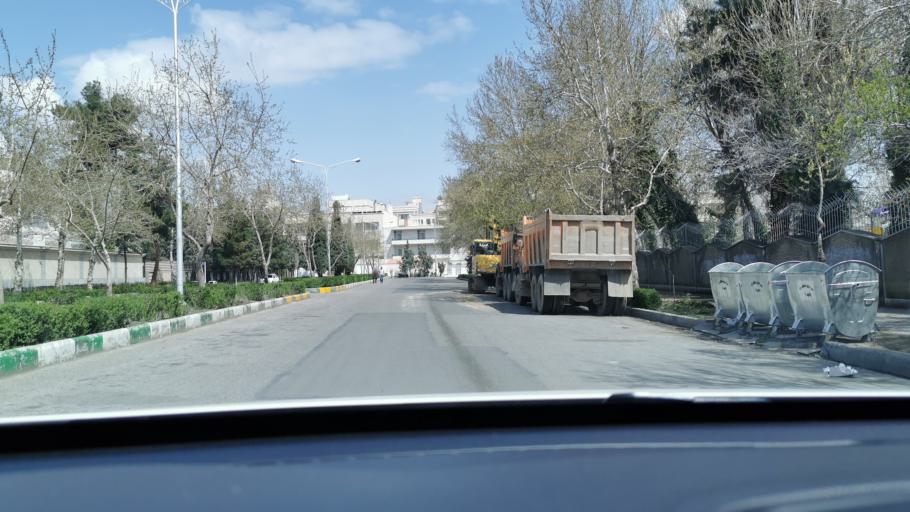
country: IR
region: Razavi Khorasan
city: Mashhad
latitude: 36.3195
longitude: 59.5307
